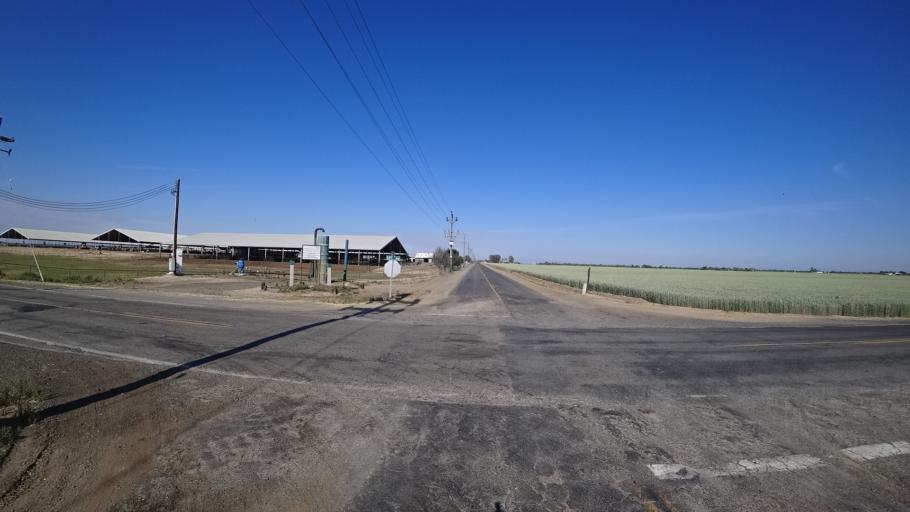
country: US
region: California
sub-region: Kings County
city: Armona
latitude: 36.2256
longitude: -119.7087
